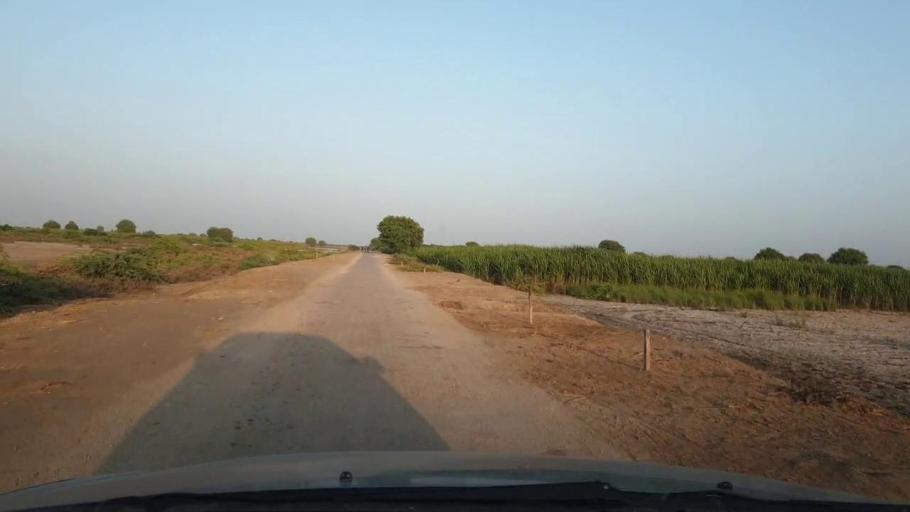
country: PK
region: Sindh
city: Tando Ghulam Ali
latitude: 25.1108
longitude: 68.9527
